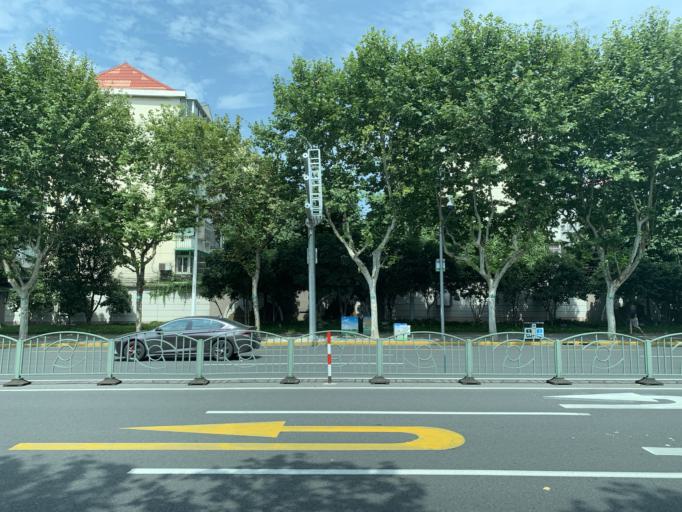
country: CN
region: Shanghai Shi
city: Pudong
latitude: 31.2359
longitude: 121.5185
